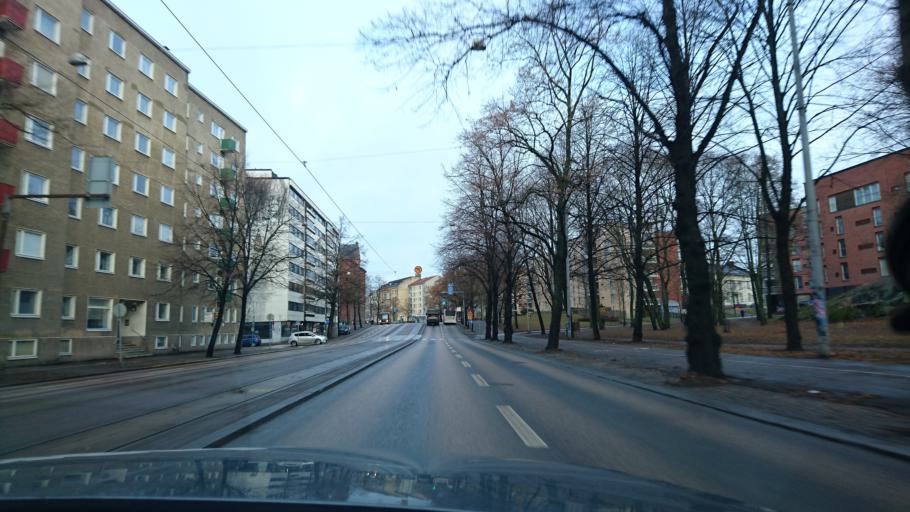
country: FI
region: Uusimaa
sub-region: Helsinki
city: Helsinki
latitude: 60.1912
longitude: 24.9646
